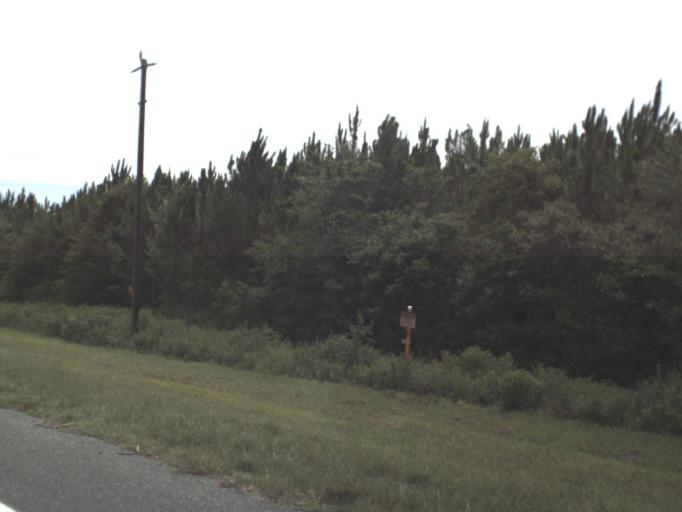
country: US
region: Florida
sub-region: Taylor County
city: Perry
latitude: 30.0890
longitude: -83.4957
